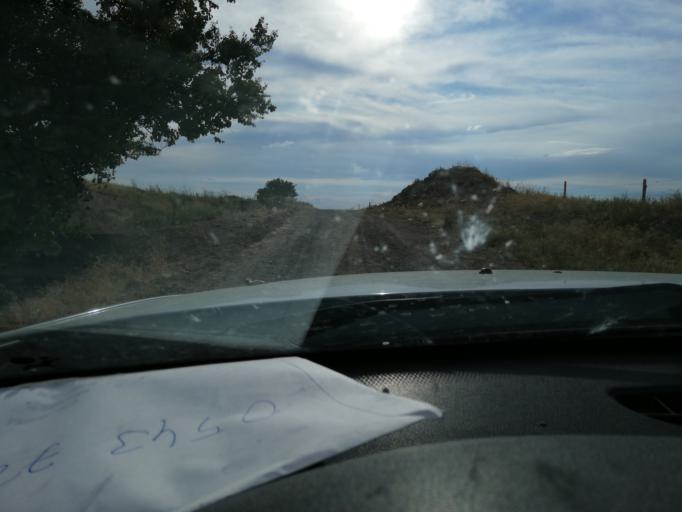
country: TR
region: Kirsehir
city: Kirsehir
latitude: 39.0030
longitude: 34.1234
